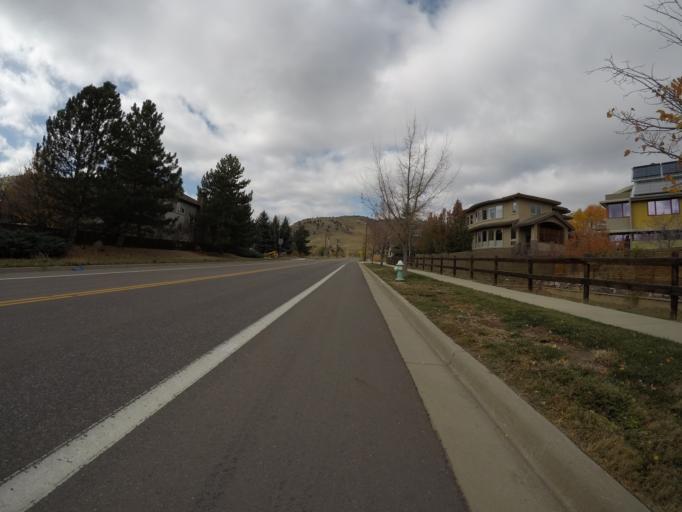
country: US
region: Colorado
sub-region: Boulder County
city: Boulder
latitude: 40.0623
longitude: -105.2871
